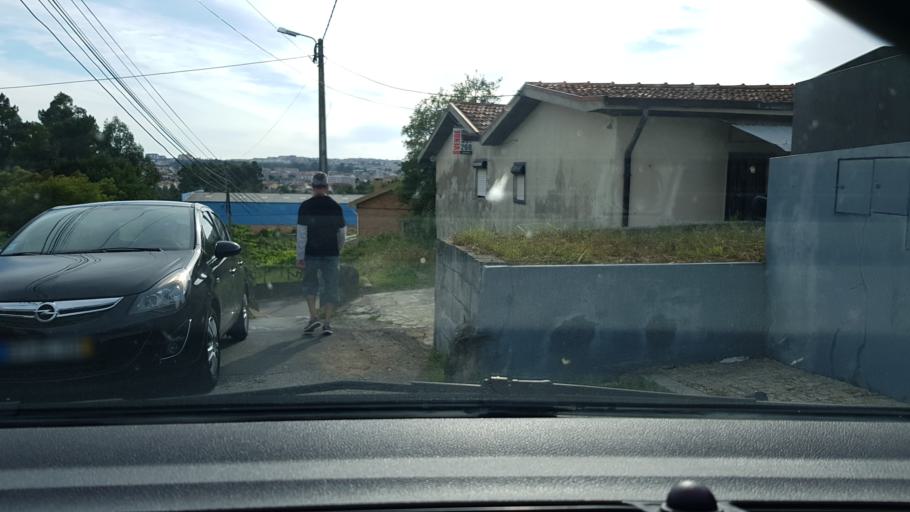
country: PT
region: Porto
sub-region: Gondomar
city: Baguim do Monte
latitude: 41.1927
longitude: -8.5442
